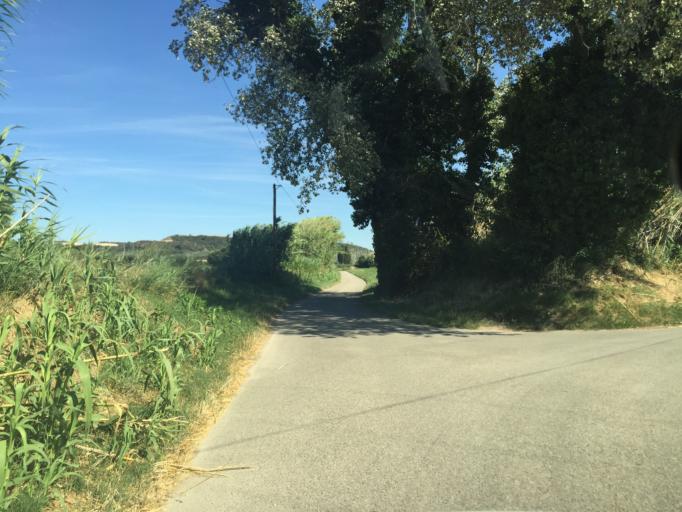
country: FR
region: Provence-Alpes-Cote d'Azur
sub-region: Departement du Vaucluse
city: Caderousse
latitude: 44.0899
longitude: 4.7656
